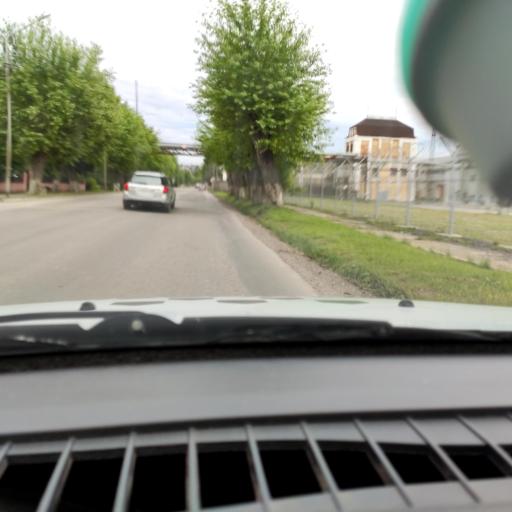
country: RU
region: Perm
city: Chusovoy
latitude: 58.2940
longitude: 57.8145
